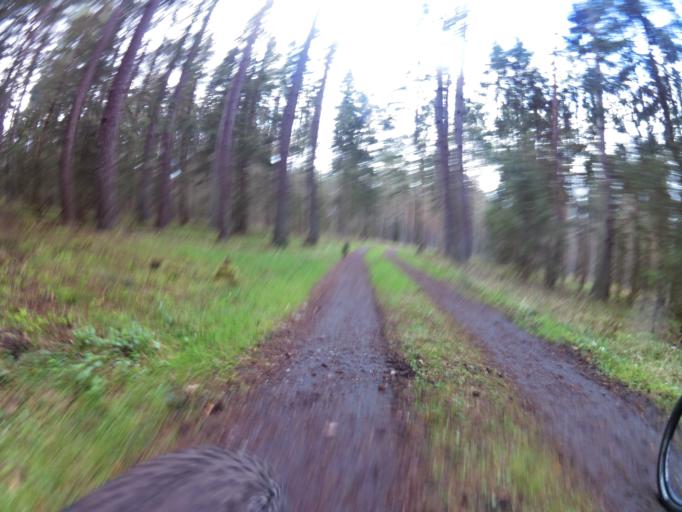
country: PL
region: Pomeranian Voivodeship
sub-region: Powiat slupski
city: Kepice
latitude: 54.3022
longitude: 16.8300
